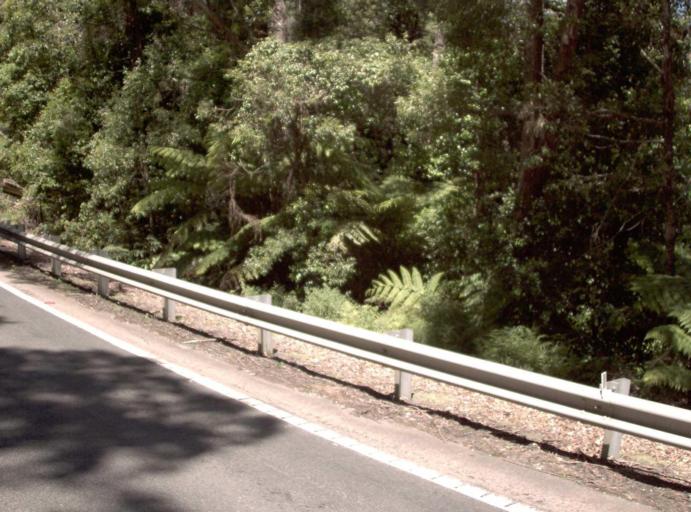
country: AU
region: New South Wales
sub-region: Bombala
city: Bombala
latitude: -37.6083
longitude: 148.8956
